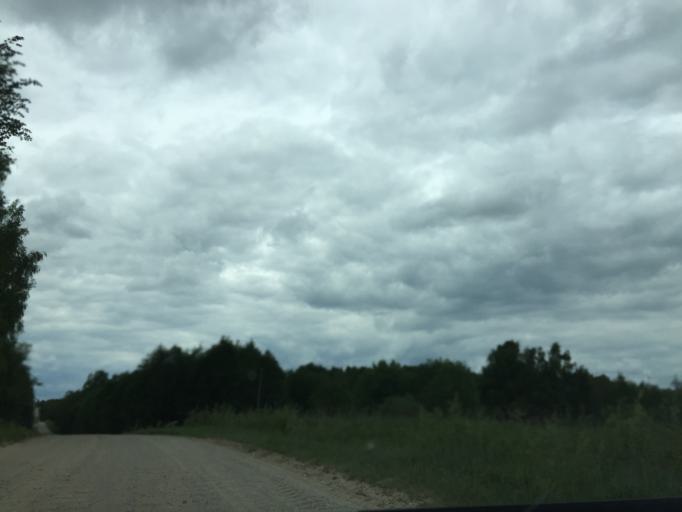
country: LV
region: Dagda
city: Dagda
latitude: 55.9962
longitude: 27.6103
